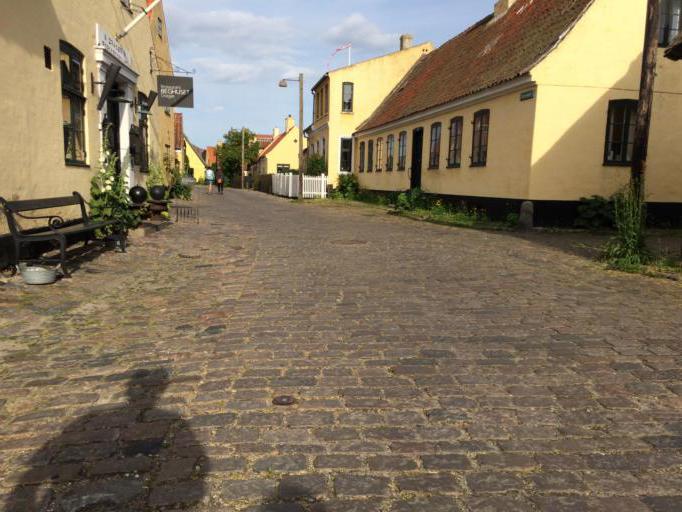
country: DK
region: Capital Region
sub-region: Dragor Kommune
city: Dragor
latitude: 55.5933
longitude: 12.6719
